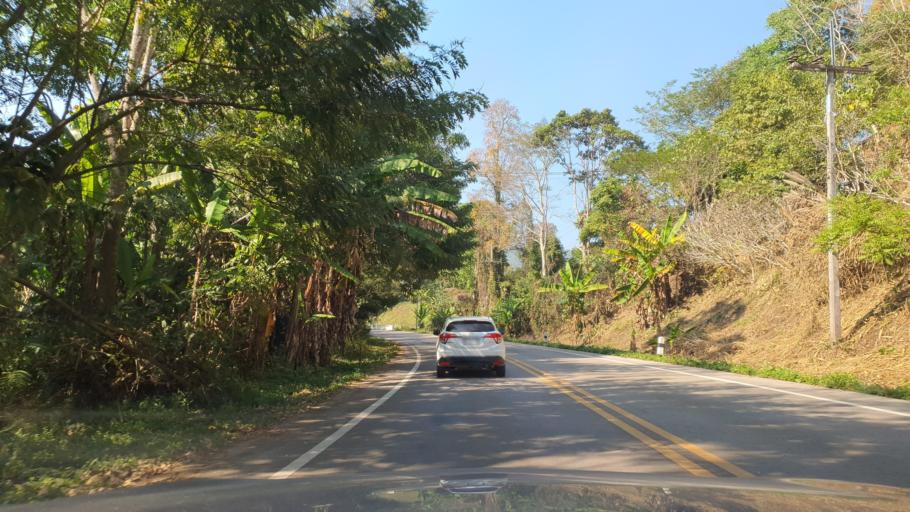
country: TH
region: Chiang Rai
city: Mae Lao
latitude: 19.8640
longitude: 99.6516
